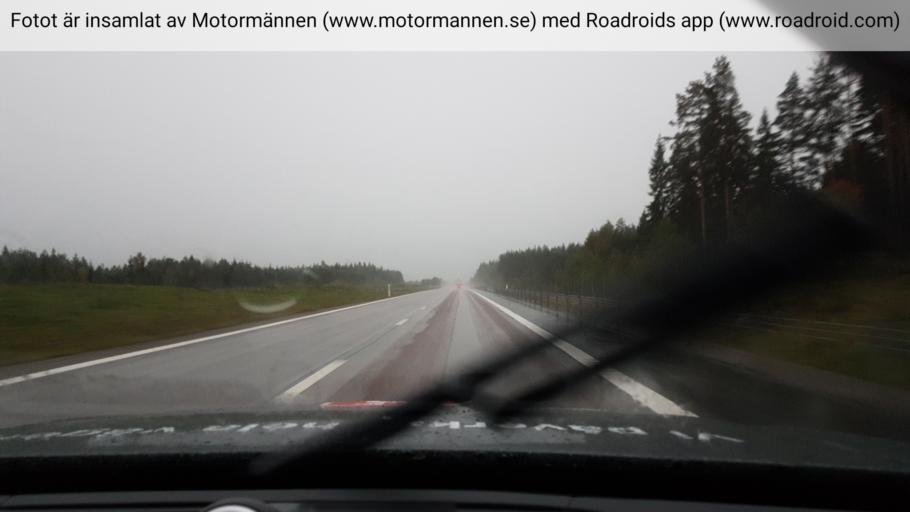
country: SE
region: Uppsala
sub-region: Tierps Kommun
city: Tierp
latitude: 60.2513
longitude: 17.5001
